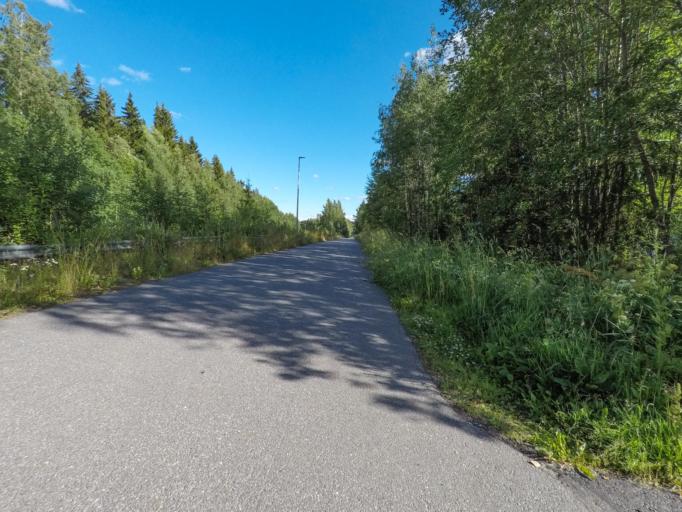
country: FI
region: South Karelia
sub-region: Lappeenranta
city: Lappeenranta
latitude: 61.0910
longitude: 28.1411
